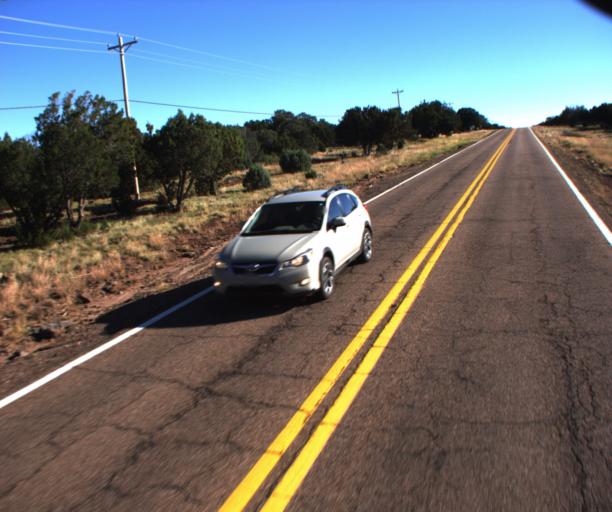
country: US
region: Arizona
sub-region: Navajo County
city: White Mountain Lake
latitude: 34.3043
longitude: -109.7830
